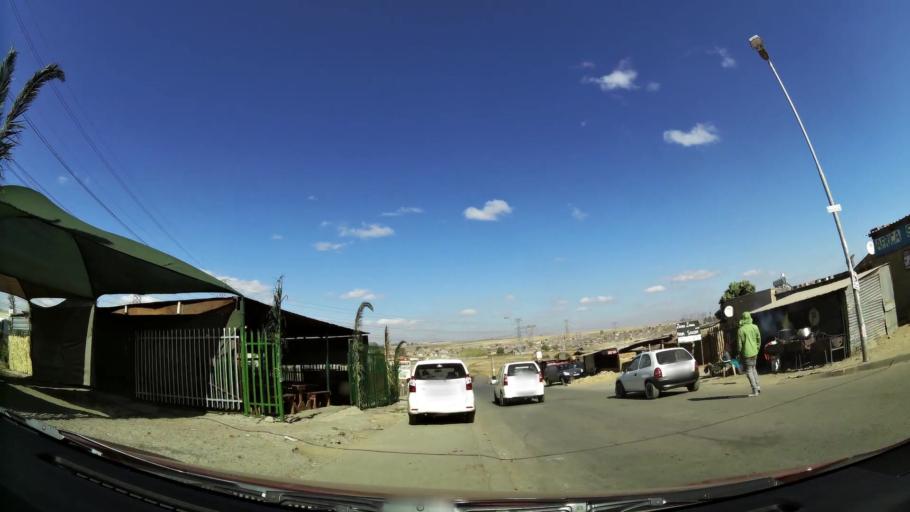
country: ZA
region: Gauteng
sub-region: City of Johannesburg Metropolitan Municipality
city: Modderfontein
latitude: -26.0361
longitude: 28.1607
